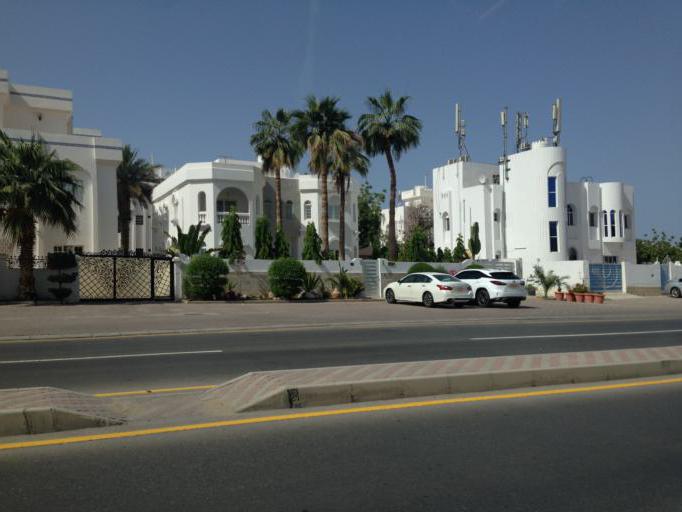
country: OM
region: Muhafazat Masqat
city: Bawshar
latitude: 23.5966
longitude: 58.4074
